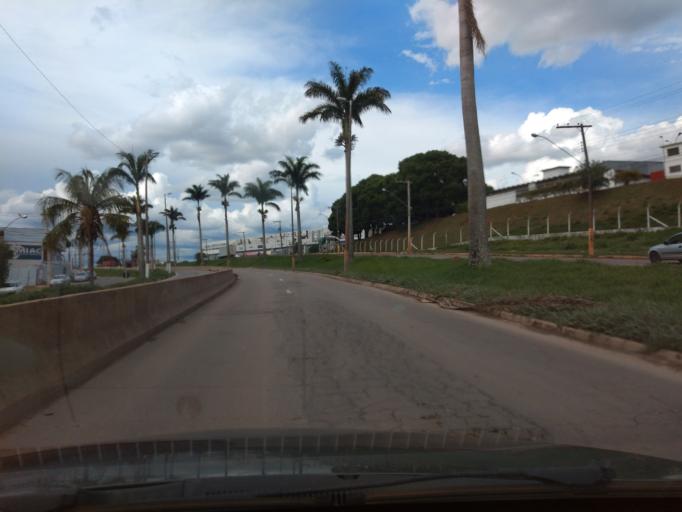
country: BR
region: Minas Gerais
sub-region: Varginha
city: Varginha
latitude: -21.5913
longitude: -45.4377
